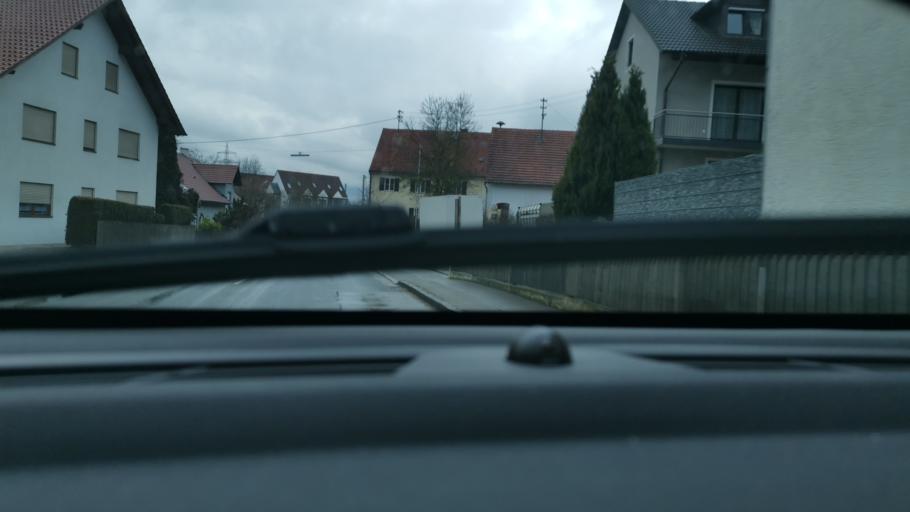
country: DE
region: Bavaria
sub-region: Swabia
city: Rehling
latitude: 48.4406
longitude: 10.9382
